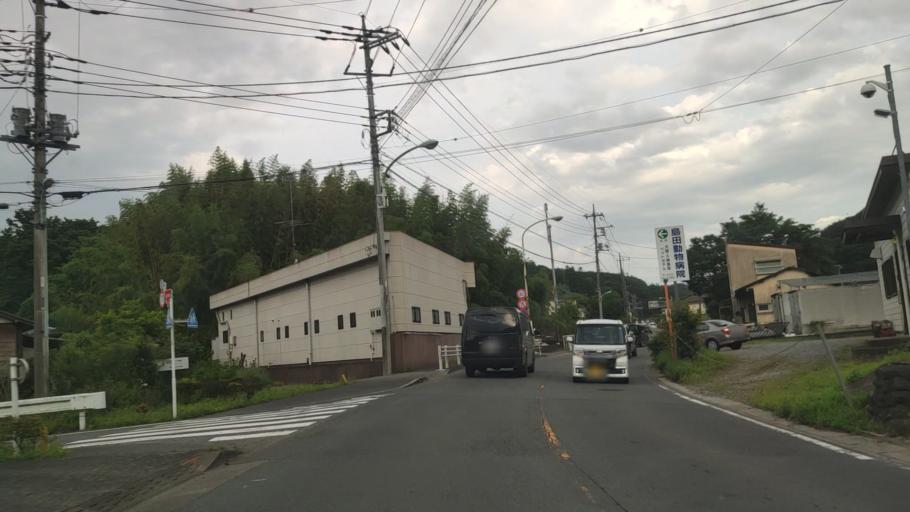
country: JP
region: Saitama
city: Hanno
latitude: 35.8213
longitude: 139.2906
